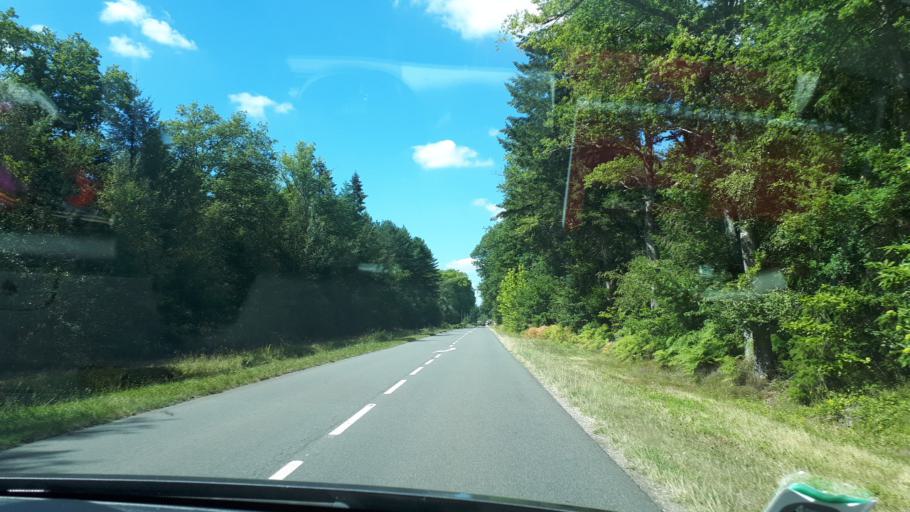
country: FR
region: Centre
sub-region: Departement du Loir-et-Cher
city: Neung-sur-Beuvron
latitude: 47.5333
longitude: 1.8143
